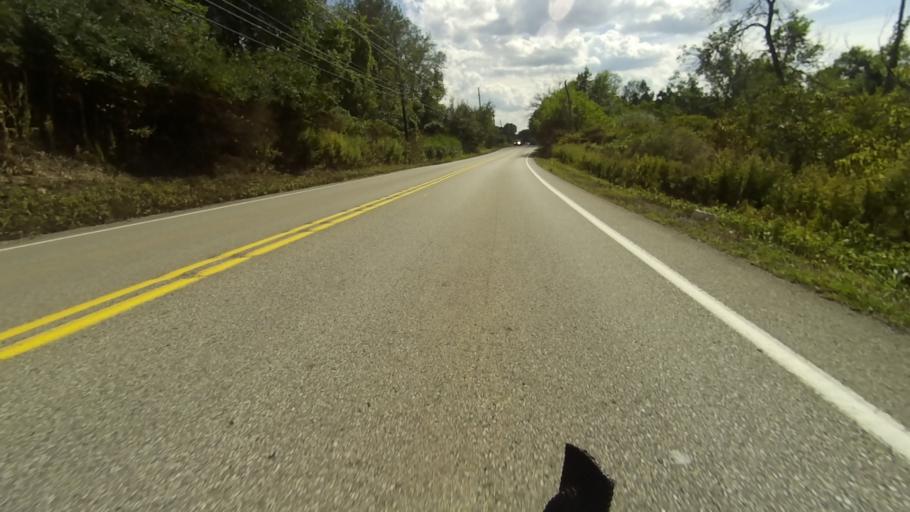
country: US
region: Pennsylvania
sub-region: Blair County
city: Greenwood
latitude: 40.5650
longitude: -78.3545
